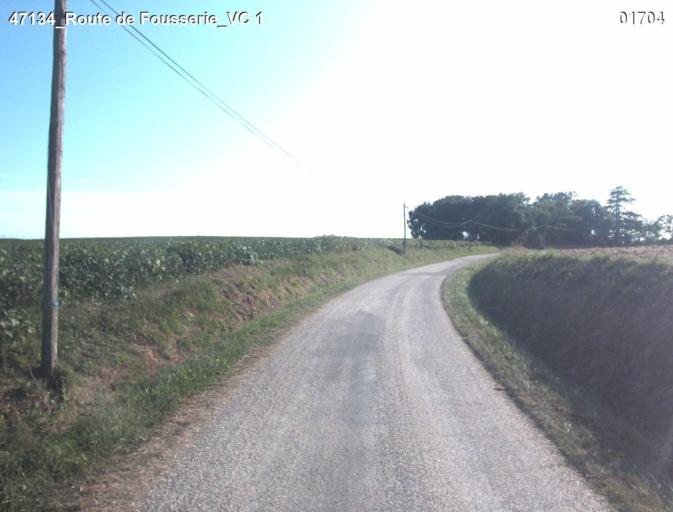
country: FR
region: Aquitaine
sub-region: Departement du Lot-et-Garonne
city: Mezin
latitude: 44.0310
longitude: 0.2872
